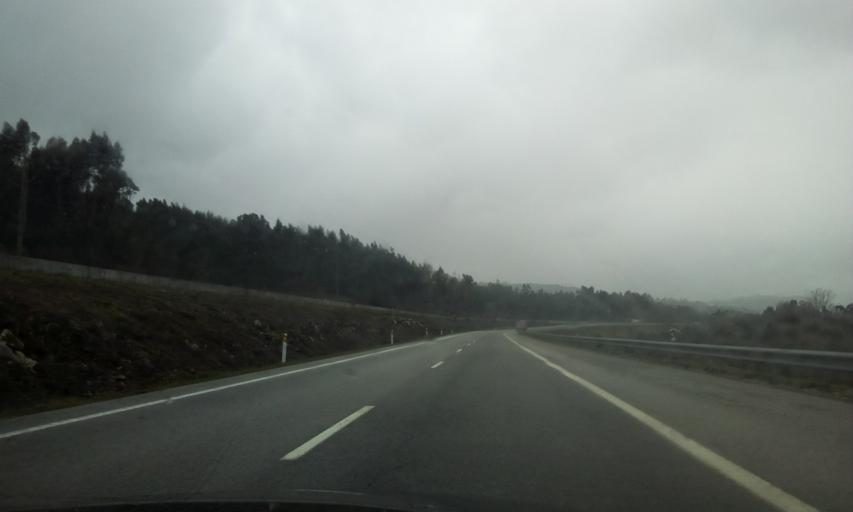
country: PT
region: Viseu
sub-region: Mangualde
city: Mangualde
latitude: 40.6135
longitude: -7.6646
